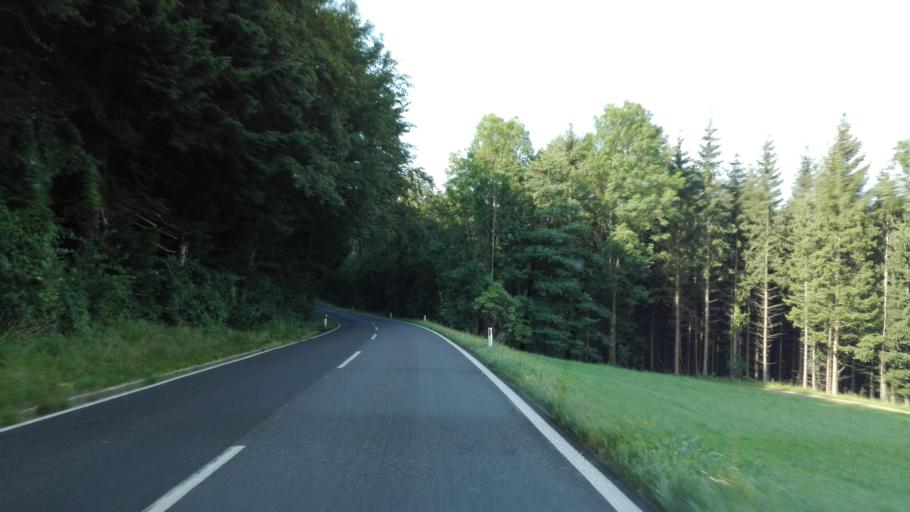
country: AT
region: Lower Austria
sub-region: Politischer Bezirk Lilienfeld
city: Rohrbach an der Goelsen
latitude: 48.0700
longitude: 15.7595
